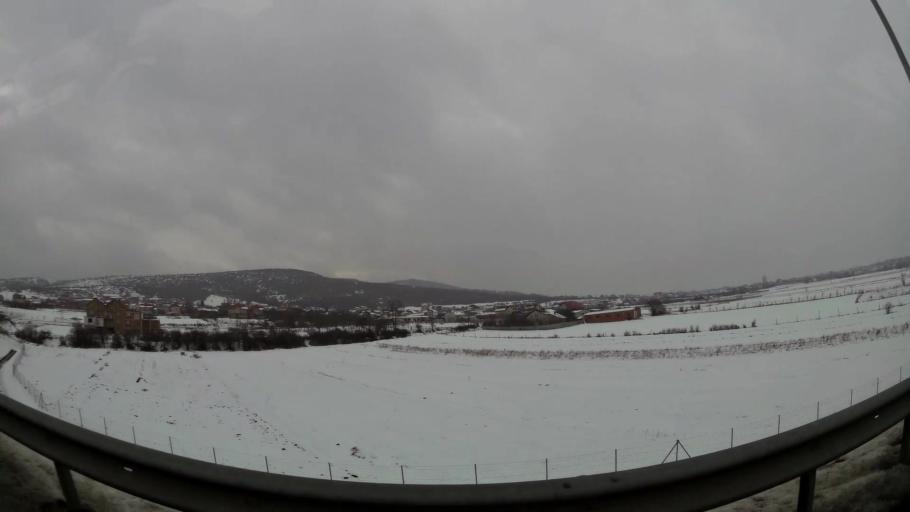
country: XK
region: Pristina
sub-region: Komuna e Prishtines
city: Pristina
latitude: 42.7313
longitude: 21.1398
